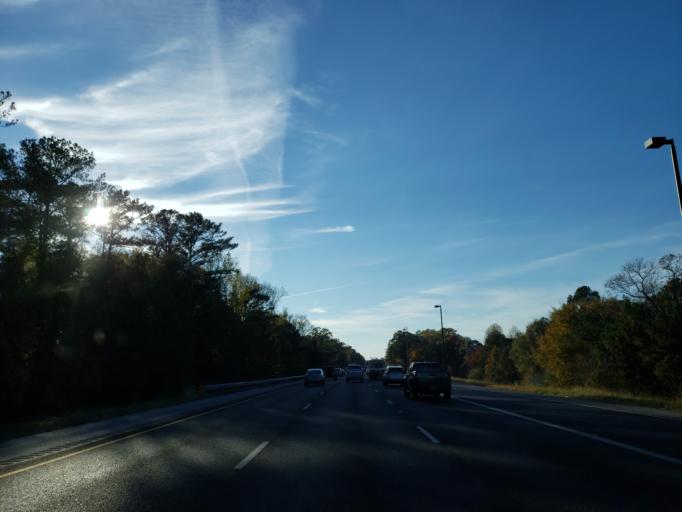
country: US
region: Alabama
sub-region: Tuscaloosa County
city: Vance
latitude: 33.1894
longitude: -87.2689
